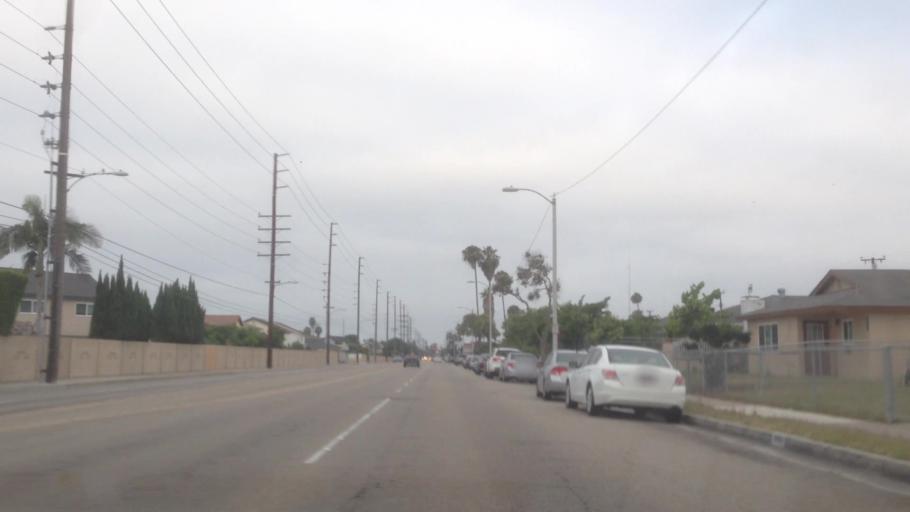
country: US
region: California
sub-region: Orange County
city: Midway City
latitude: 33.7376
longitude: -117.9743
